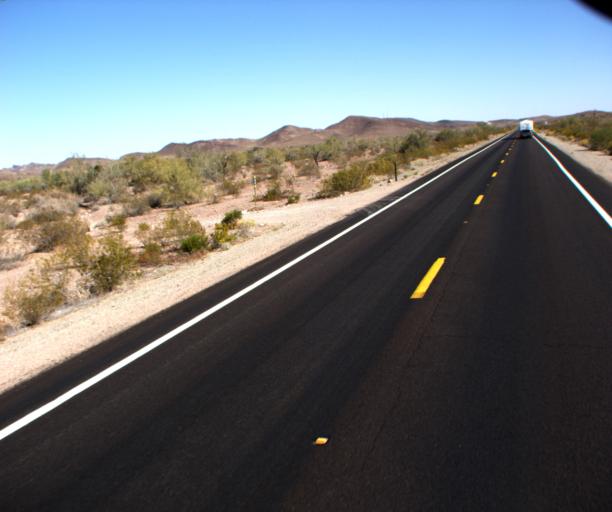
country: US
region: Arizona
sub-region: La Paz County
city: Quartzsite
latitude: 33.2103
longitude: -114.2637
